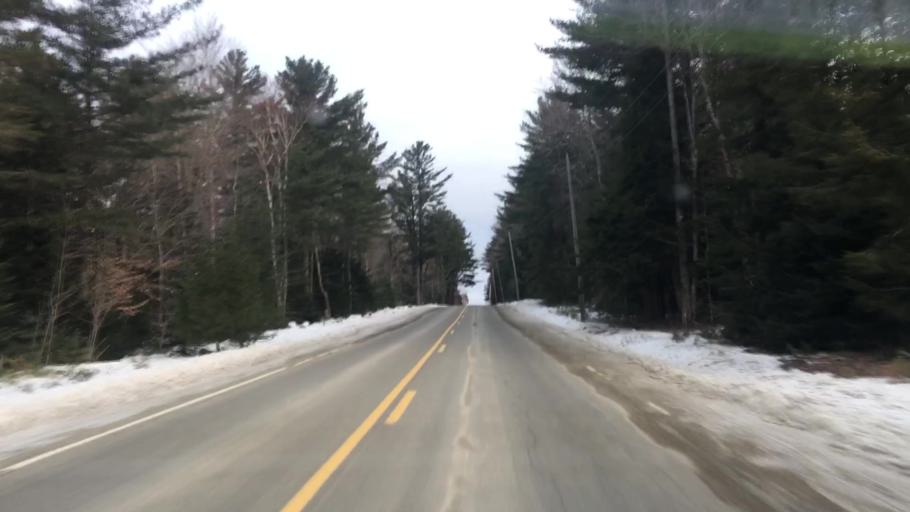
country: US
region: Maine
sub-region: Hancock County
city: Franklin
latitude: 44.7640
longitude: -68.3252
